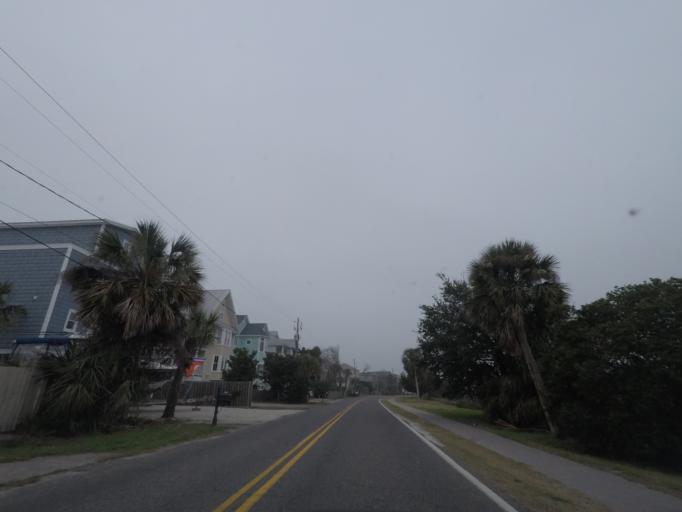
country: US
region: South Carolina
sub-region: Charleston County
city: Seabrook Island
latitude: 32.4920
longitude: -80.3312
